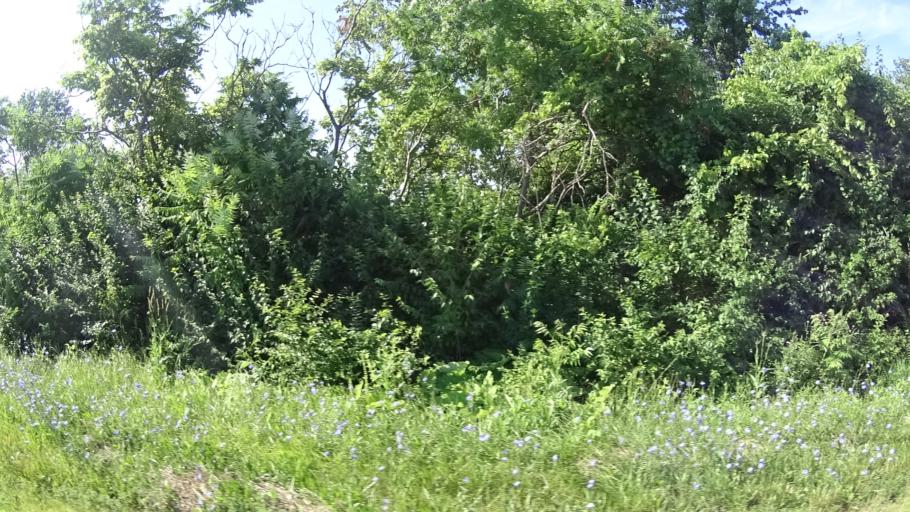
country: US
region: Ohio
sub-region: Erie County
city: Sandusky
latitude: 41.4692
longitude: -82.8114
